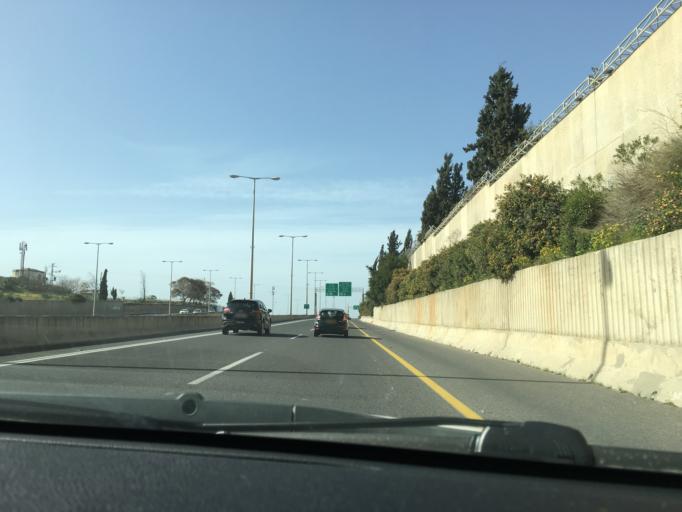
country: IL
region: Tel Aviv
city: Ramat HaSharon
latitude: 32.1318
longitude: 34.8392
